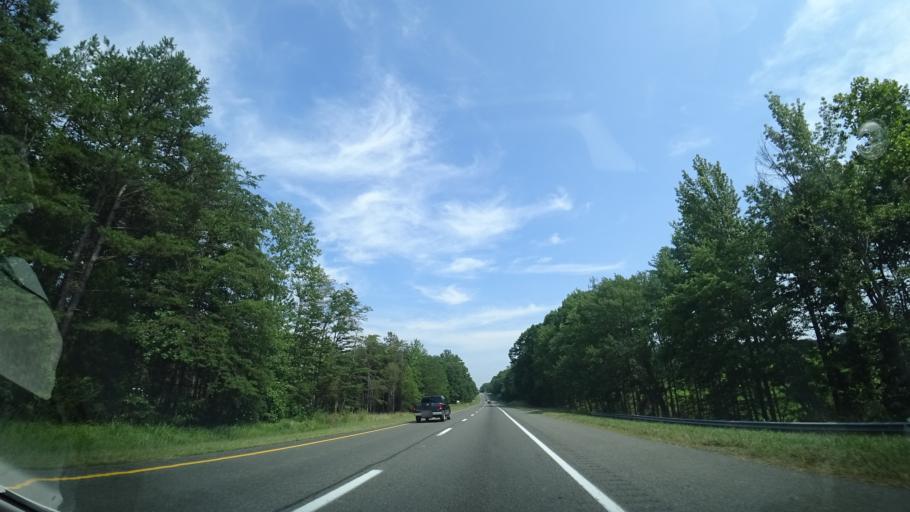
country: US
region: Virginia
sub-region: Louisa County
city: Louisa
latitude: 37.8918
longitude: -78.0401
